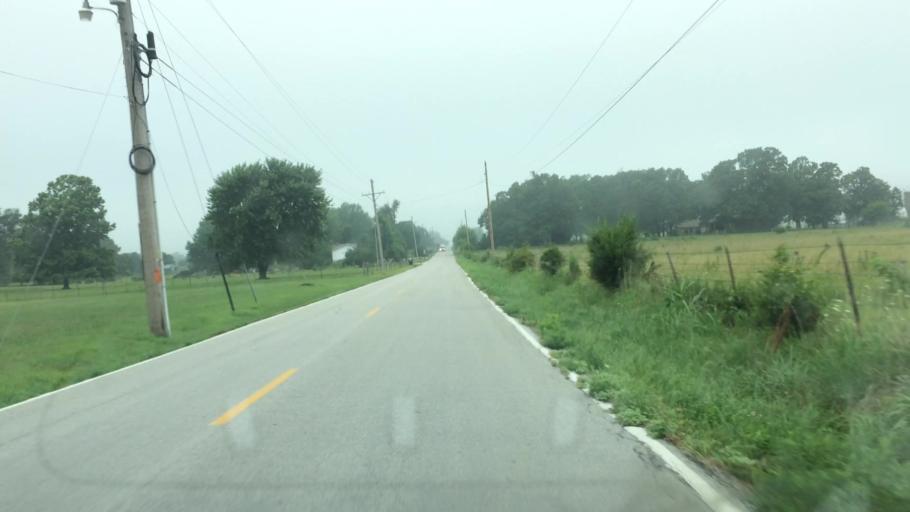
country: US
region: Missouri
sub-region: Greene County
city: Strafford
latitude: 37.2712
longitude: -93.1503
